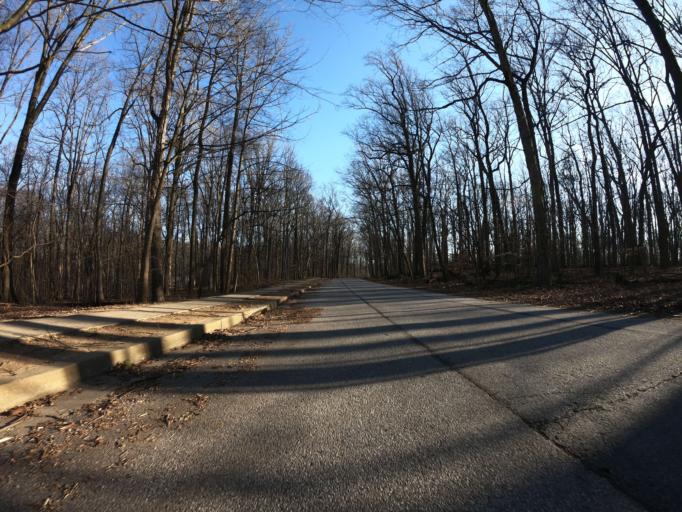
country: US
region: Maryland
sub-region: Howard County
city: Ilchester
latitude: 39.2491
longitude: -76.7443
